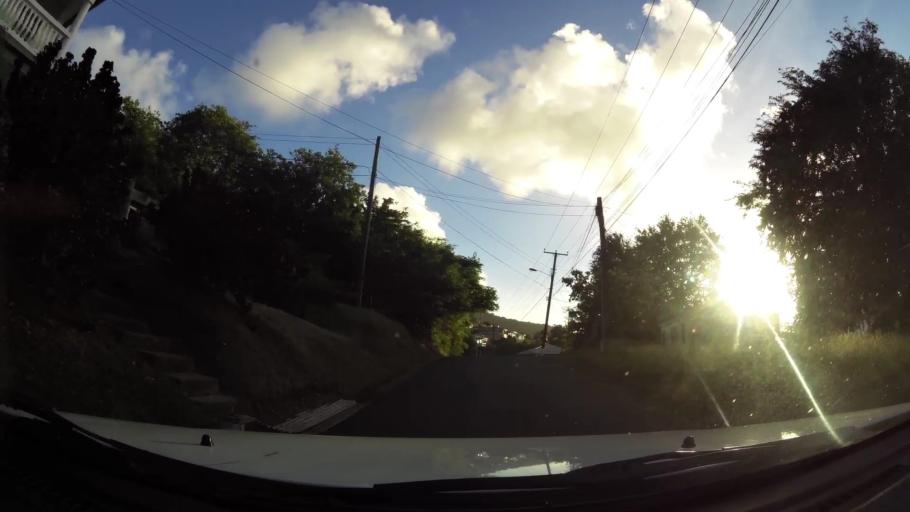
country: LC
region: Gros-Islet
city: Gros Islet
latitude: 14.0655
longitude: -60.9378
